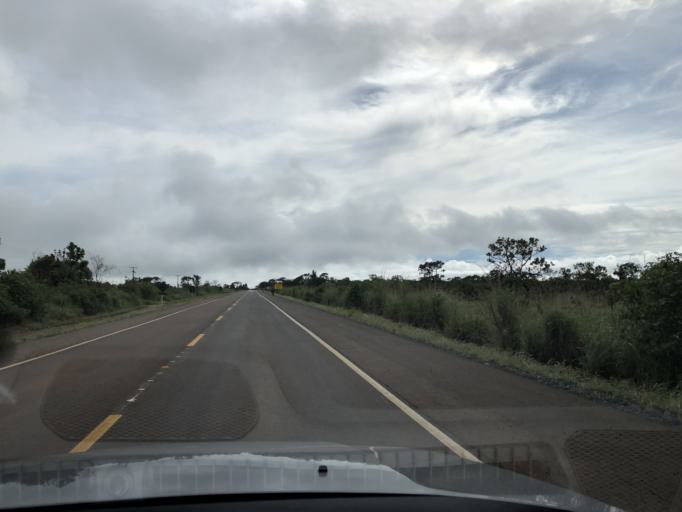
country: BR
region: Federal District
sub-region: Brasilia
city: Brasilia
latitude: -15.6210
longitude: -48.0623
